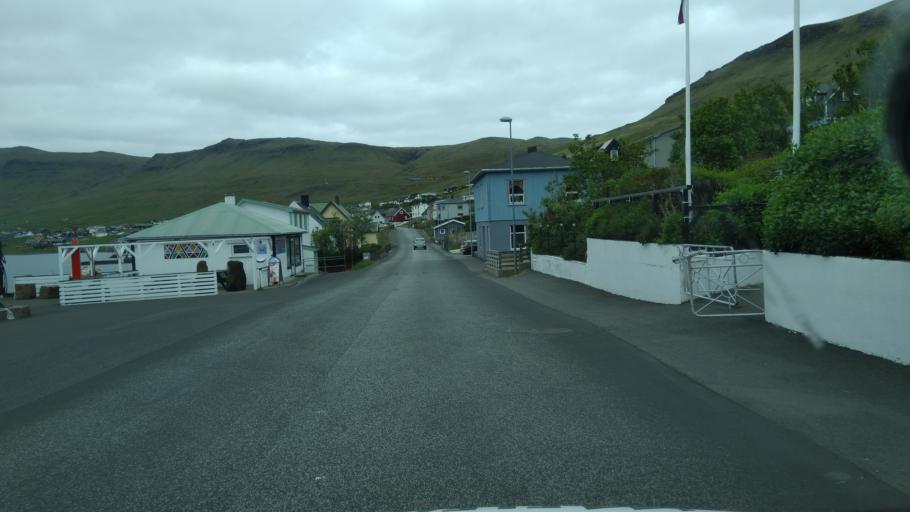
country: FO
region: Suduroy
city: Tvoroyri
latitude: 61.5596
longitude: -6.8237
